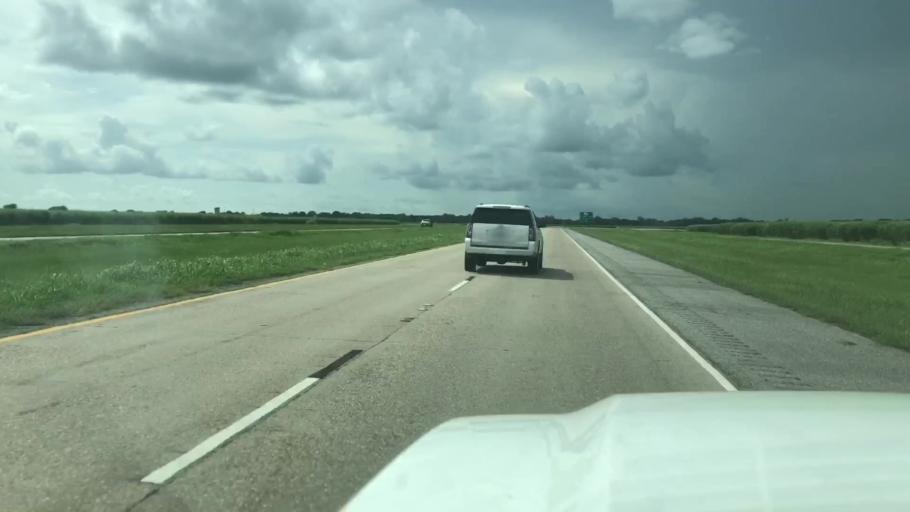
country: US
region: Louisiana
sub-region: Saint Mary Parish
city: Franklin
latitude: 29.7542
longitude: -91.4515
